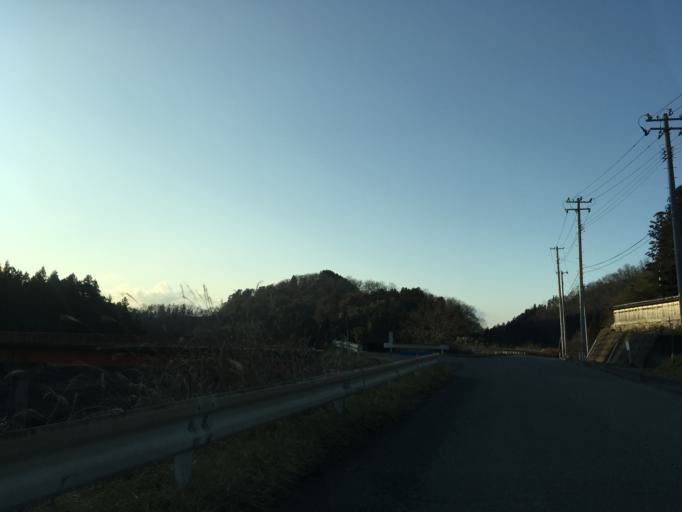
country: JP
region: Iwate
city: Ichinoseki
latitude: 38.8022
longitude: 141.2326
